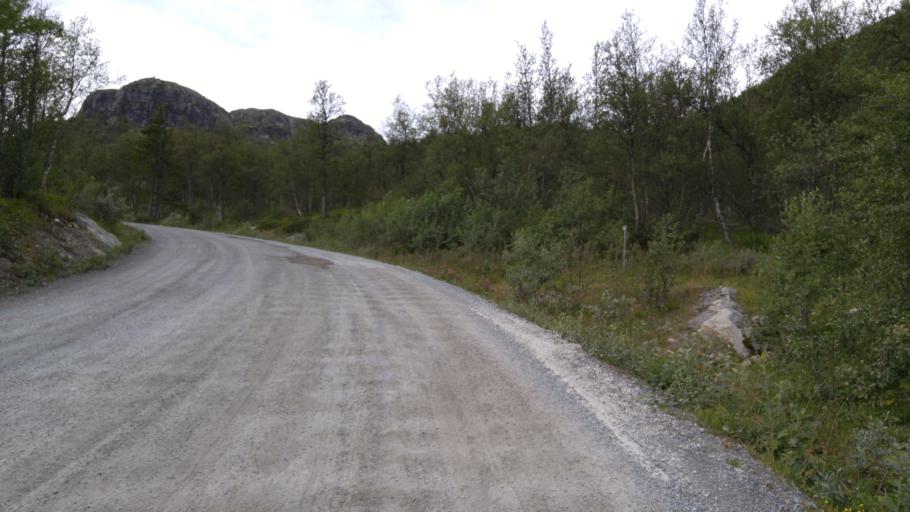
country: NO
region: Buskerud
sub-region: Hemsedal
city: Hemsedal
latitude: 60.8558
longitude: 8.4902
